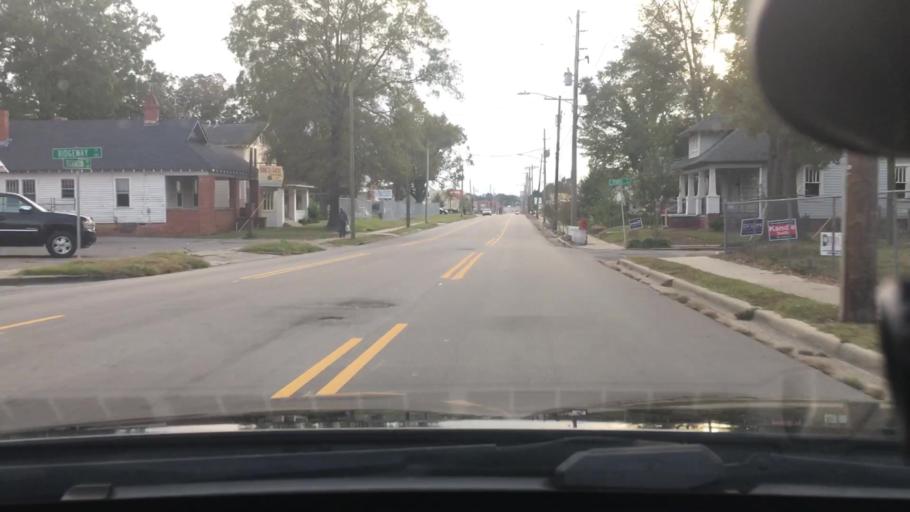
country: US
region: North Carolina
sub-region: Pitt County
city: Greenville
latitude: 35.6045
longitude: -77.3852
